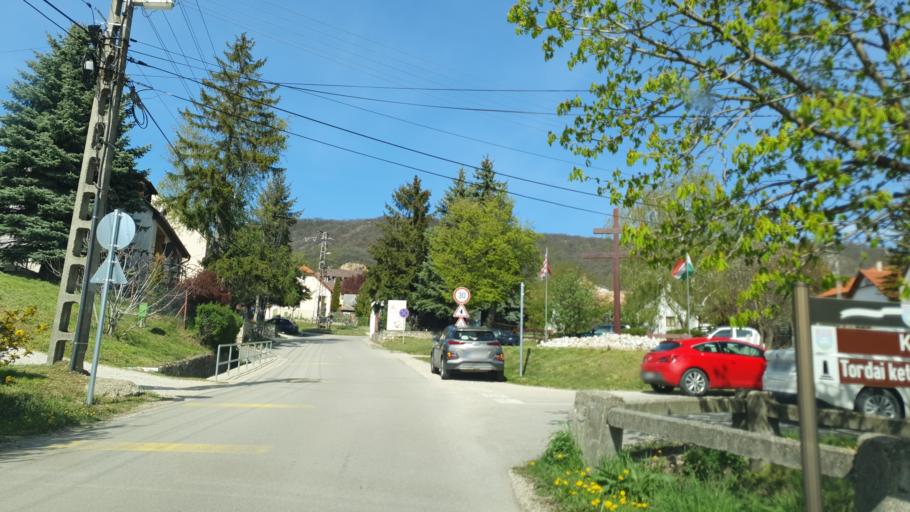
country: HU
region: Fejer
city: Bodajk
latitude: 47.3545
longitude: 18.2749
